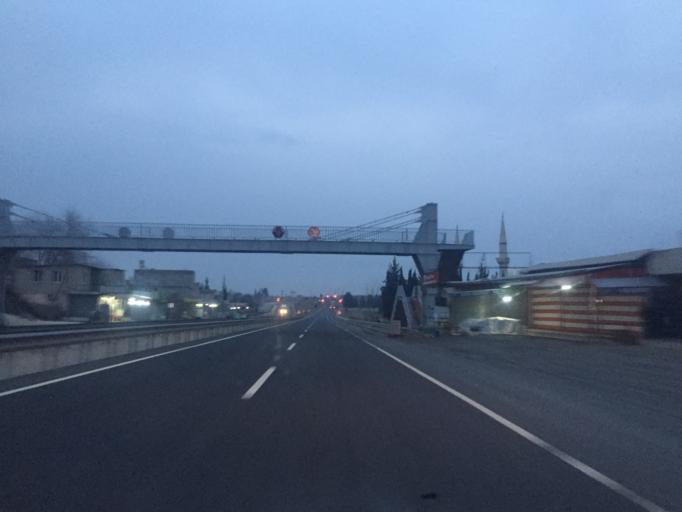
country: TR
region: Sanliurfa
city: Camlidere
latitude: 37.1542
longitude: 39.0638
